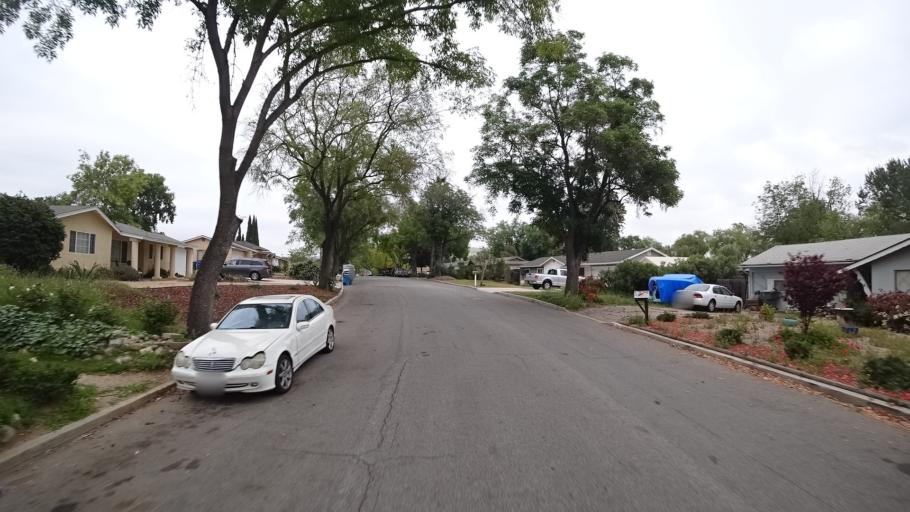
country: US
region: California
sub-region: Ventura County
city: Thousand Oaks
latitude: 34.2071
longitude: -118.8556
